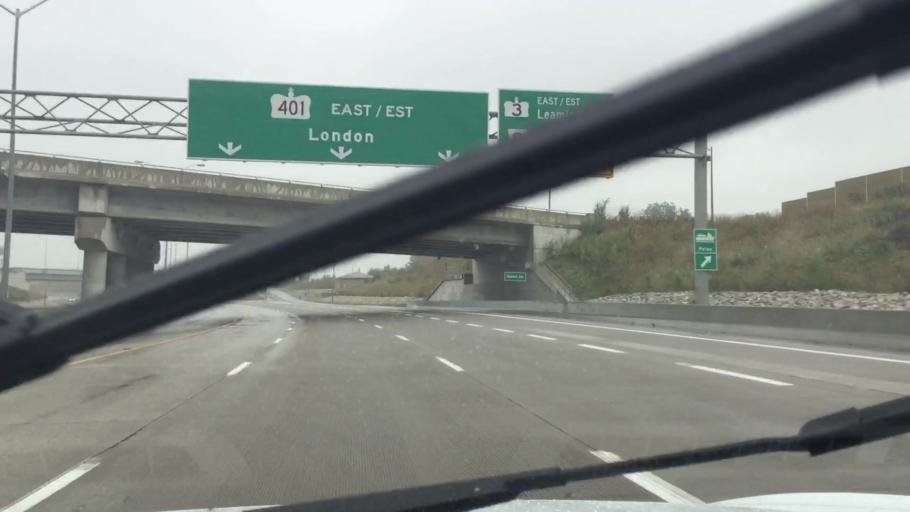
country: CA
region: Ontario
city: Windsor
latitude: 42.2345
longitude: -82.9973
